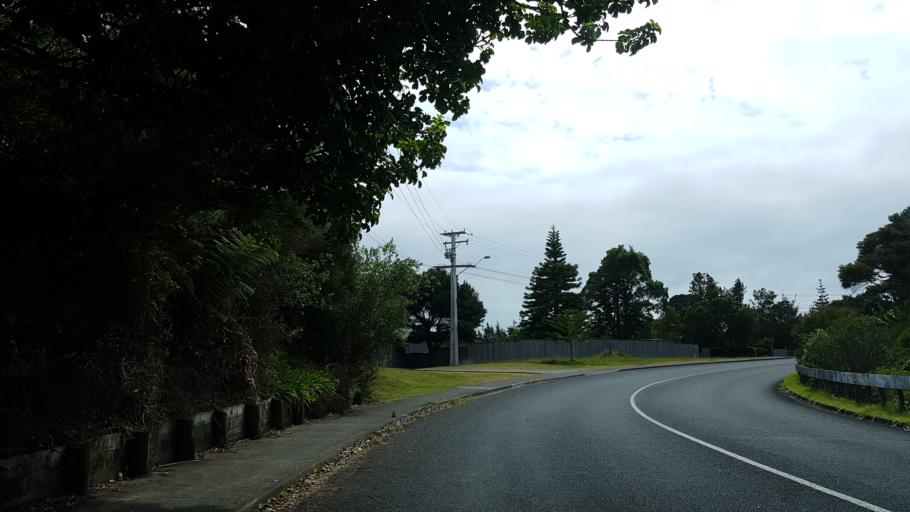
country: NZ
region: Auckland
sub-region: Auckland
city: North Shore
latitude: -36.7677
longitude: 174.7143
